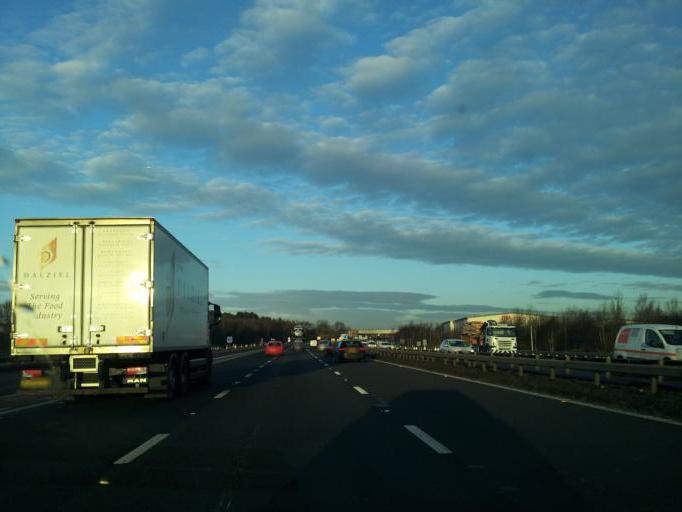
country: GB
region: England
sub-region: City and Borough of Wakefield
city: Normanton
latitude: 53.7096
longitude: -1.4067
